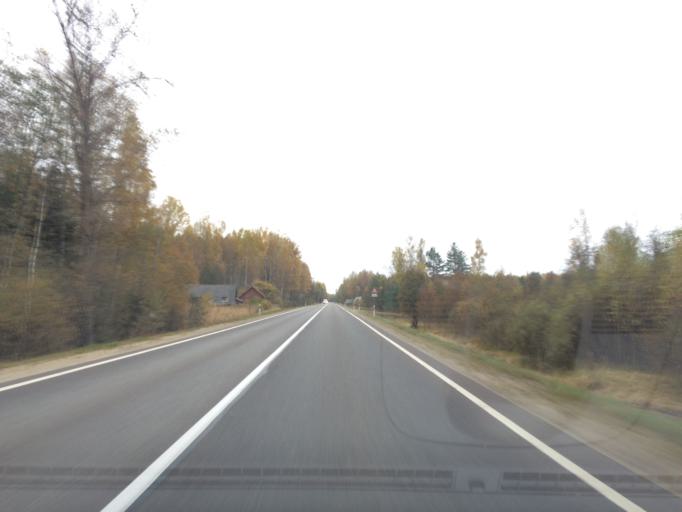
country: LV
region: Livani
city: Livani
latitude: 56.5453
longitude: 26.1191
